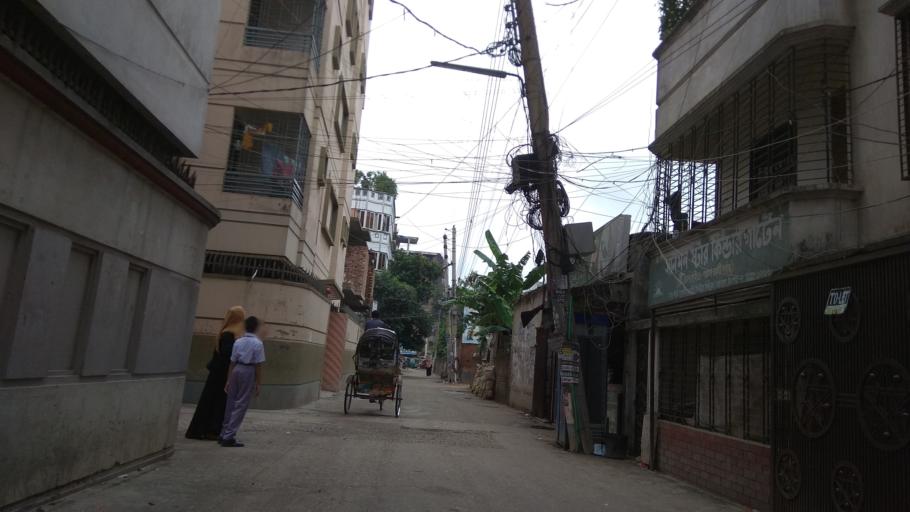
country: BD
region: Dhaka
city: Azimpur
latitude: 23.7996
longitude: 90.3600
